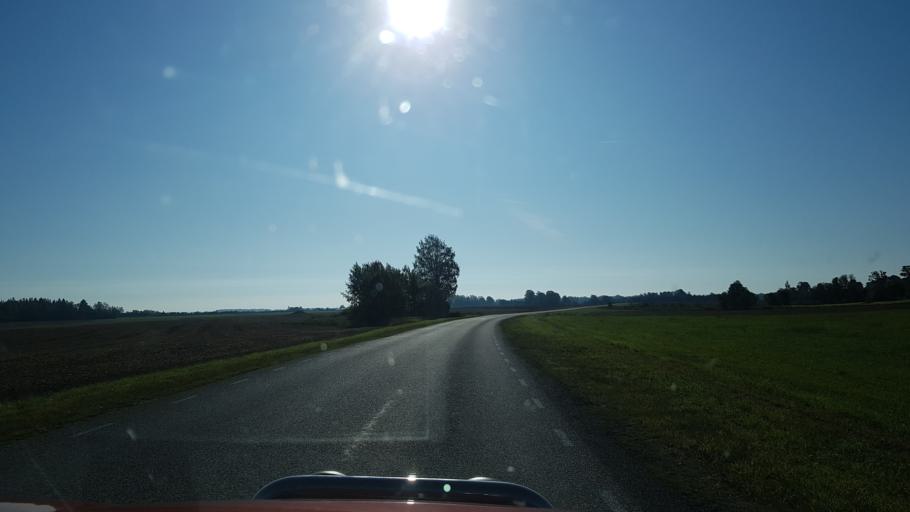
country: EE
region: Jogevamaa
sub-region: Tabivere vald
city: Tabivere
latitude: 58.6812
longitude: 26.6604
